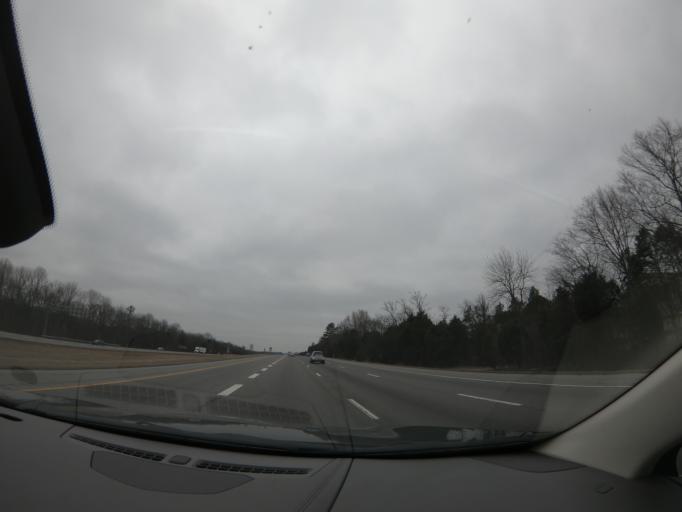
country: US
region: Tennessee
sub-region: Rutherford County
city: Smyrna
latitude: 35.9416
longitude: -86.5393
